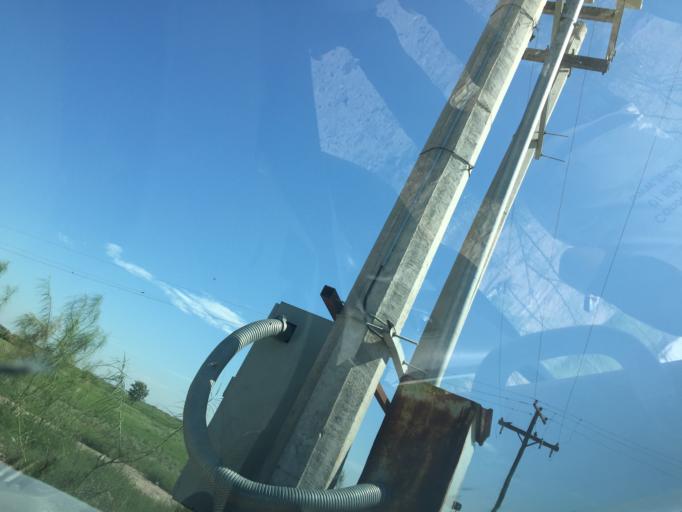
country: MX
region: Durango
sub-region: Gomez Palacio
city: San Felipe
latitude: 25.7243
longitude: -103.3767
